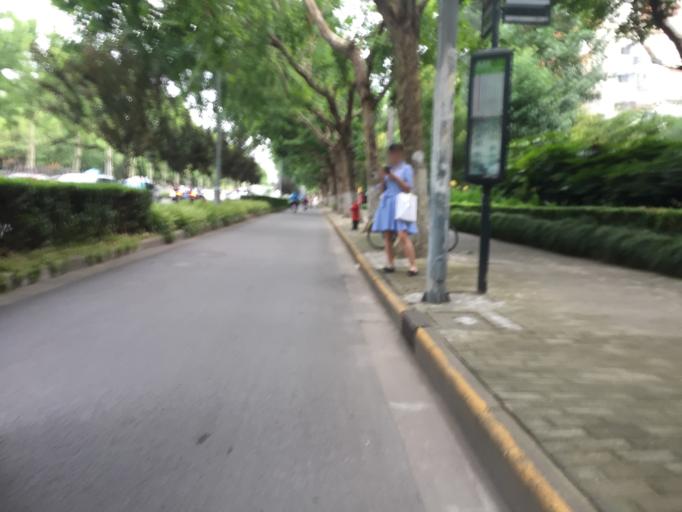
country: CN
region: Shanghai Shi
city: Huamu
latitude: 31.1842
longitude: 121.5370
